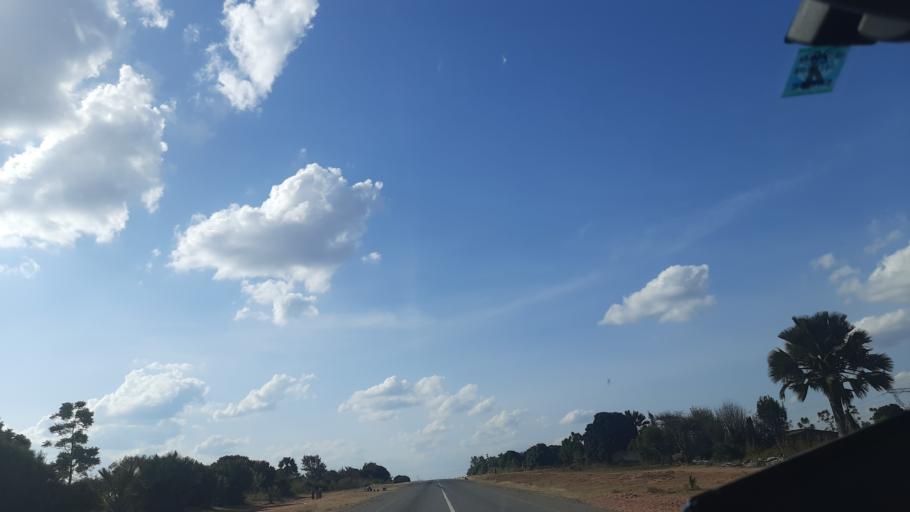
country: TZ
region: Singida
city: Ikungi
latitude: -5.0868
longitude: 34.7657
